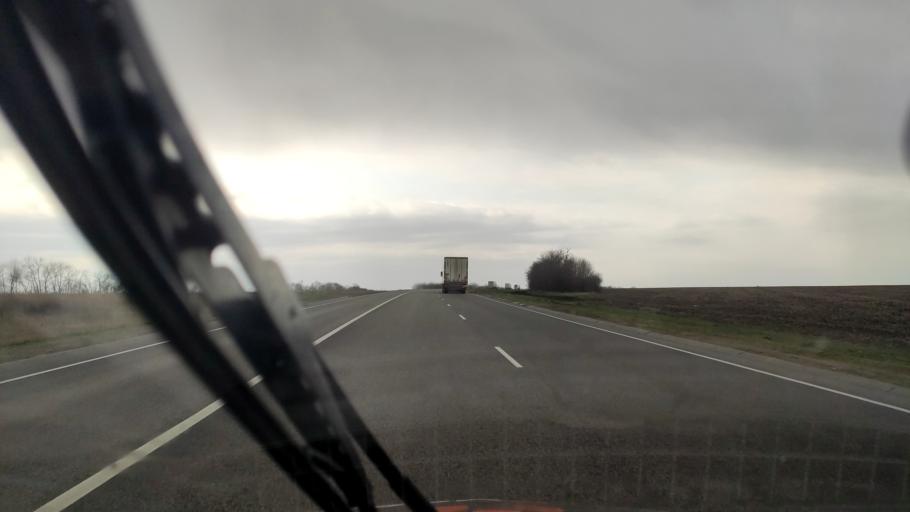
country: RU
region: Voronezj
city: Nizhnedevitsk
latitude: 51.5651
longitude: 38.3539
